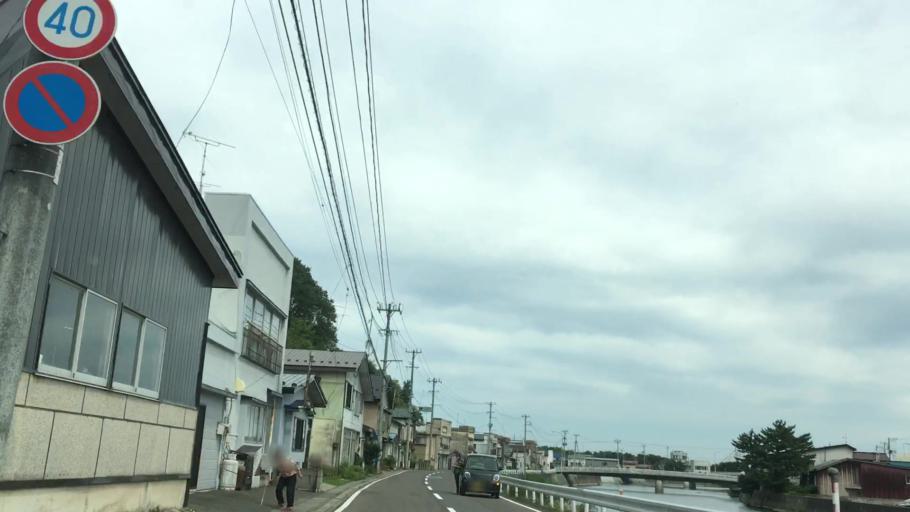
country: JP
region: Aomori
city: Shimokizukuri
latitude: 40.7750
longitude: 140.2162
